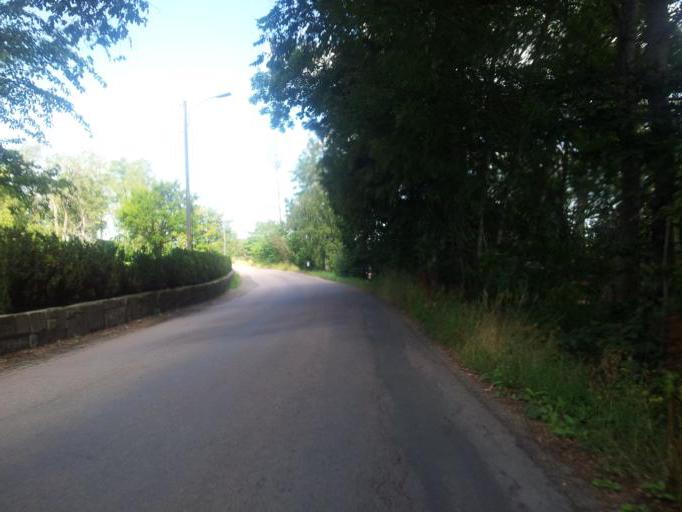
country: SE
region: Uppsala
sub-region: Uppsala Kommun
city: Gamla Uppsala
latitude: 59.8996
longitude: 17.6341
